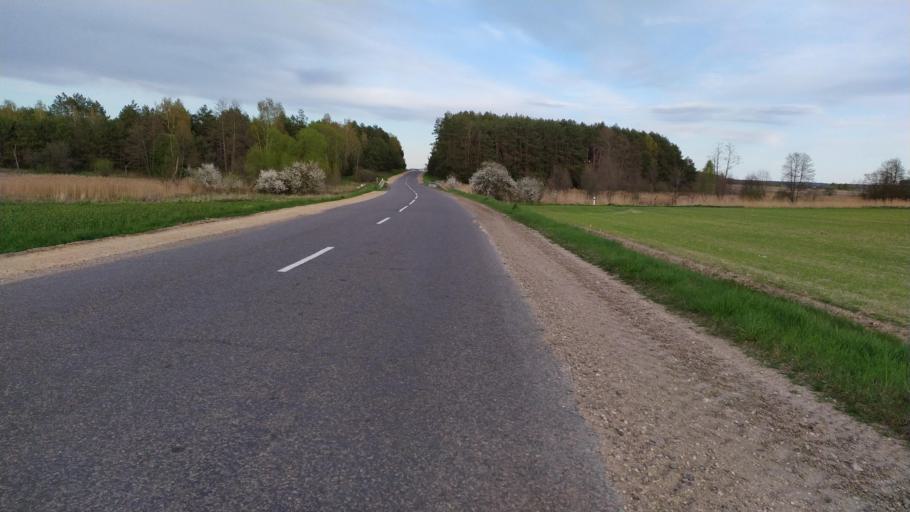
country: BY
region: Brest
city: Kamyanyets
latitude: 52.4092
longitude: 23.7304
